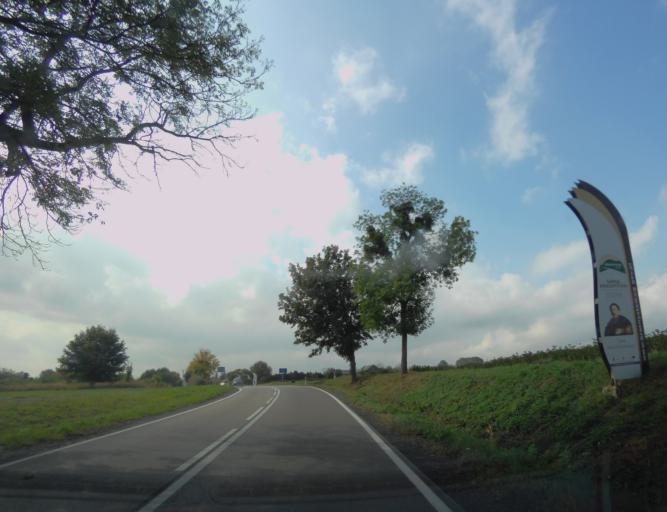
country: PL
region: Lublin Voivodeship
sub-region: Powiat krasnostawski
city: Gorzkow
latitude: 50.9710
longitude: 23.0506
